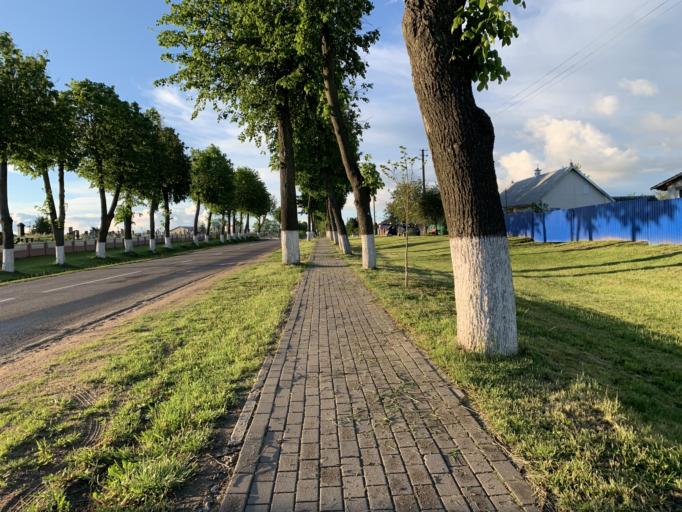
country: BY
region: Minsk
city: Nyasvizh
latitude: 53.2081
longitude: 26.6958
